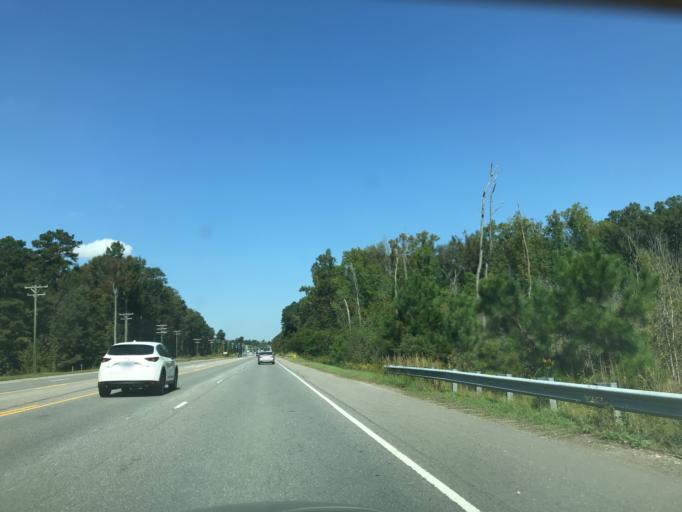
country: US
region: North Carolina
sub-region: Wake County
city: Morrisville
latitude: 35.8828
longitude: -78.8933
